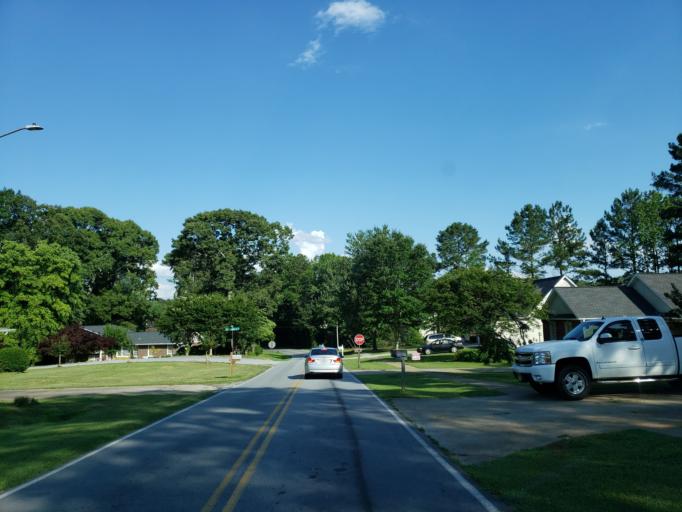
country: US
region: Georgia
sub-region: Haralson County
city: Bremen
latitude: 33.7147
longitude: -85.1365
